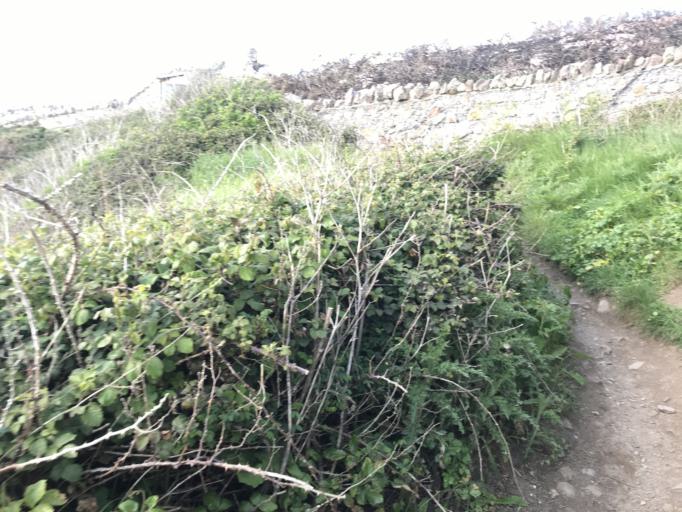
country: IE
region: Leinster
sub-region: Fingal County
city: Howth
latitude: 53.3647
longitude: -6.0864
